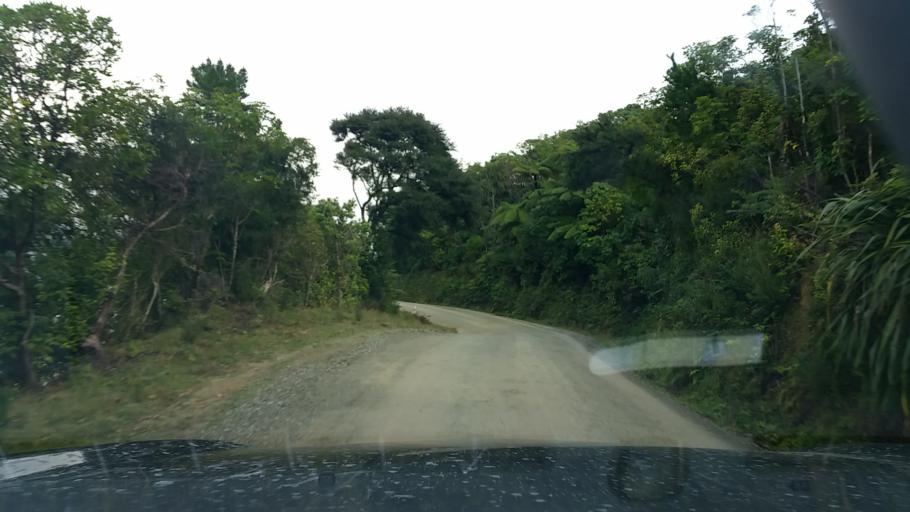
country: NZ
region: Marlborough
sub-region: Marlborough District
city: Picton
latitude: -41.1786
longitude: 174.0547
